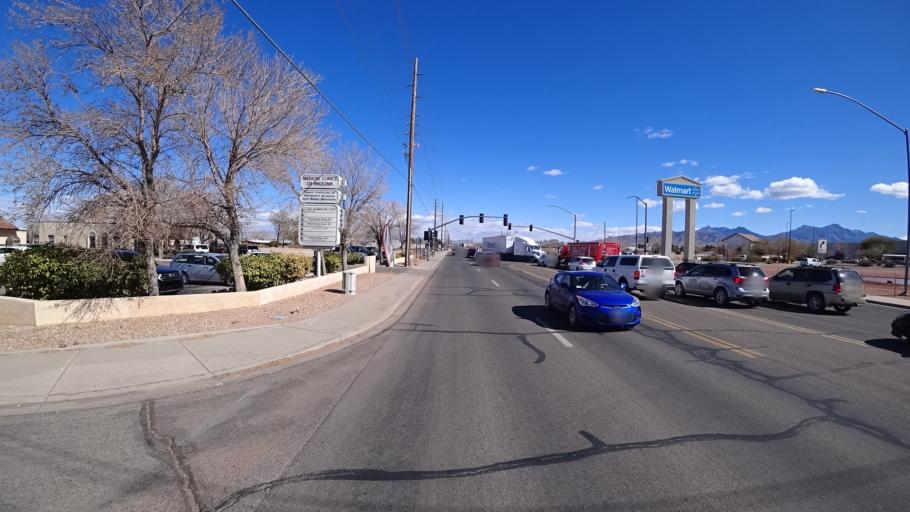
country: US
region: Arizona
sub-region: Mohave County
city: New Kingman-Butler
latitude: 35.2249
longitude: -114.0335
